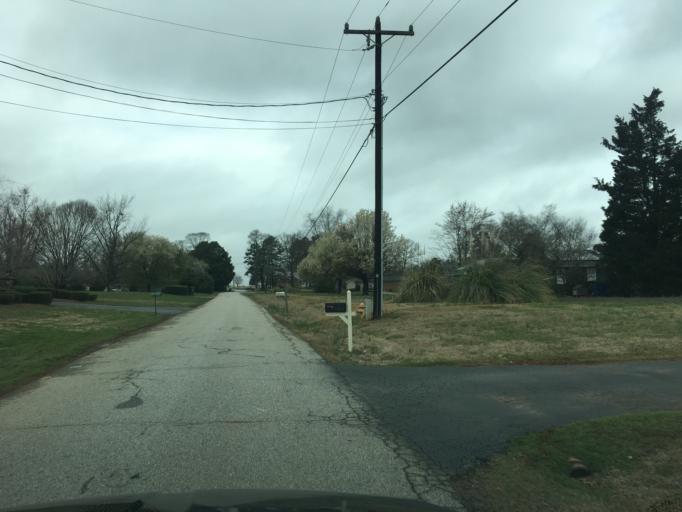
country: US
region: South Carolina
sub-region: Spartanburg County
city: Inman Mills
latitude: 35.0211
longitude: -82.1102
